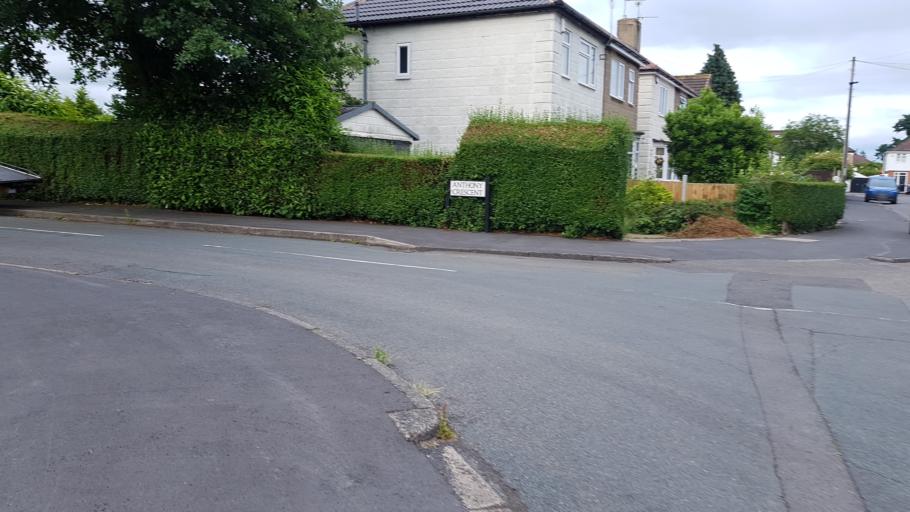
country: GB
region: England
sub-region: Derby
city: Derby
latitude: 52.8903
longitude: -1.4380
